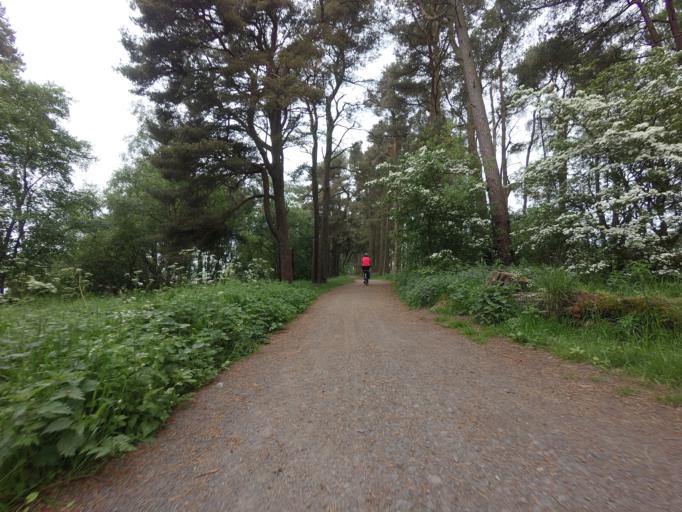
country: GB
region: Scotland
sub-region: Perth and Kinross
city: Milnathort
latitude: 56.2203
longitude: -3.3944
